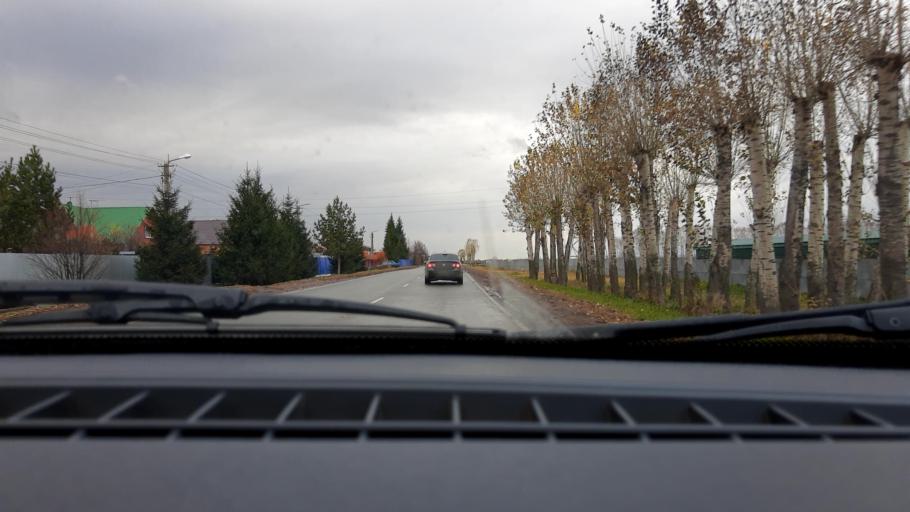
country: RU
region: Bashkortostan
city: Ufa
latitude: 54.8263
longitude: 55.9917
